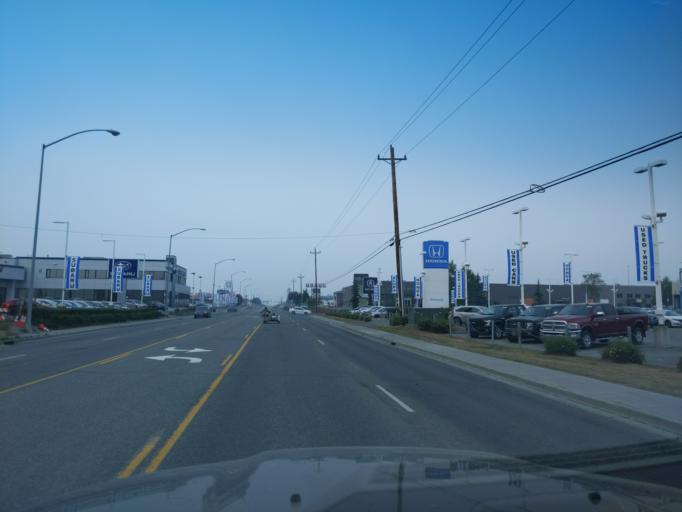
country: US
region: Alaska
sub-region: Anchorage Municipality
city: Anchorage
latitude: 61.1748
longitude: -149.8680
